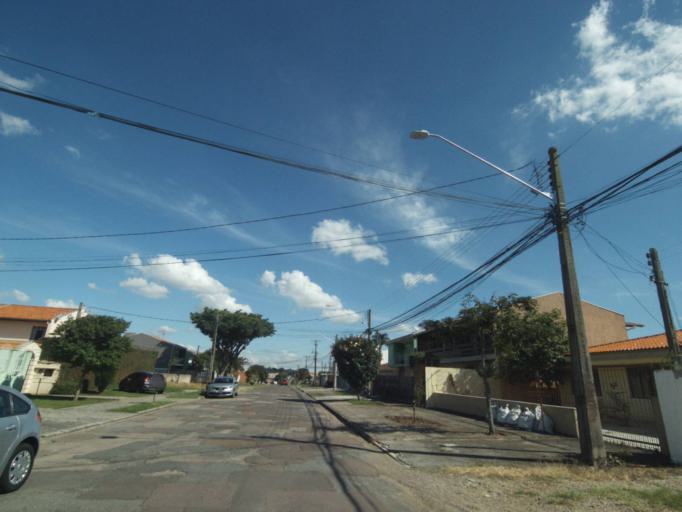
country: BR
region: Parana
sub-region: Pinhais
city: Pinhais
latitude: -25.4543
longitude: -49.2128
